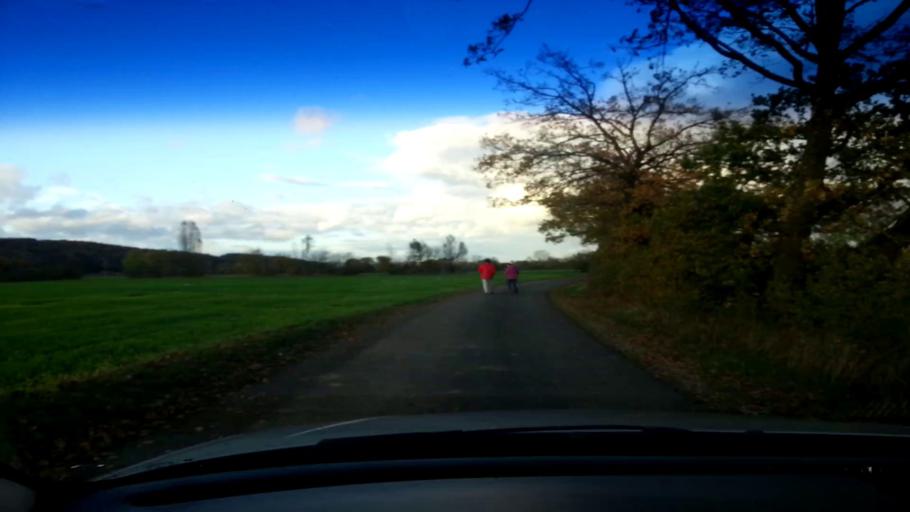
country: DE
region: Bavaria
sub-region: Upper Franconia
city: Zapfendorf
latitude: 50.0439
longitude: 10.9313
